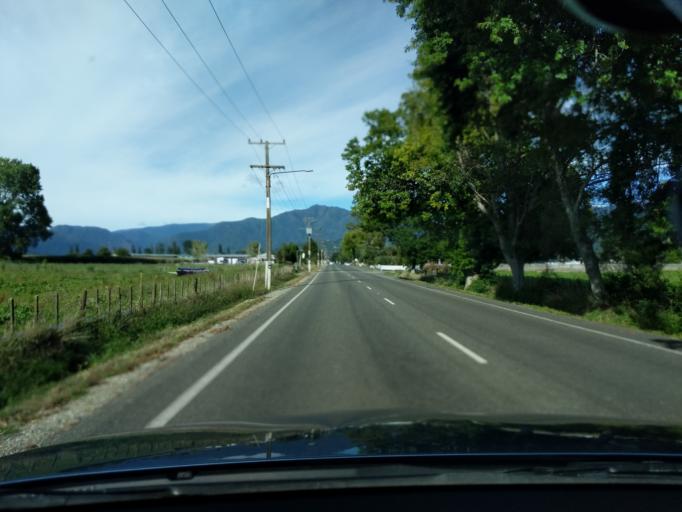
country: NZ
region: Tasman
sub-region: Tasman District
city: Takaka
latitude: -40.8560
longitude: 172.8134
